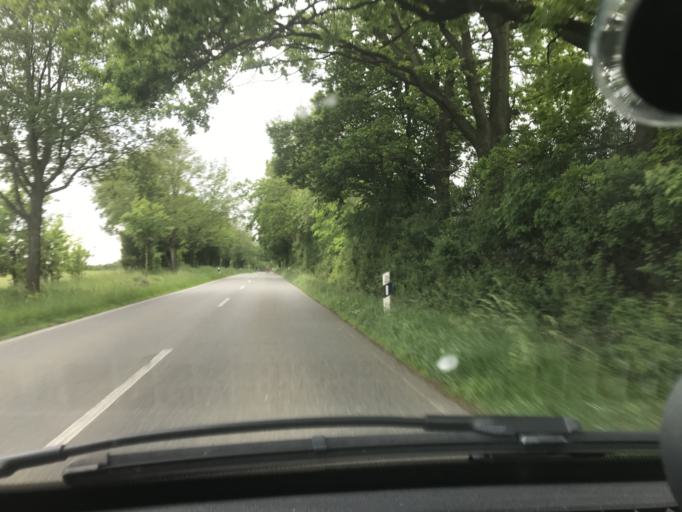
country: DE
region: Schleswig-Holstein
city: Siek
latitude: 53.6137
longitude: 10.2995
